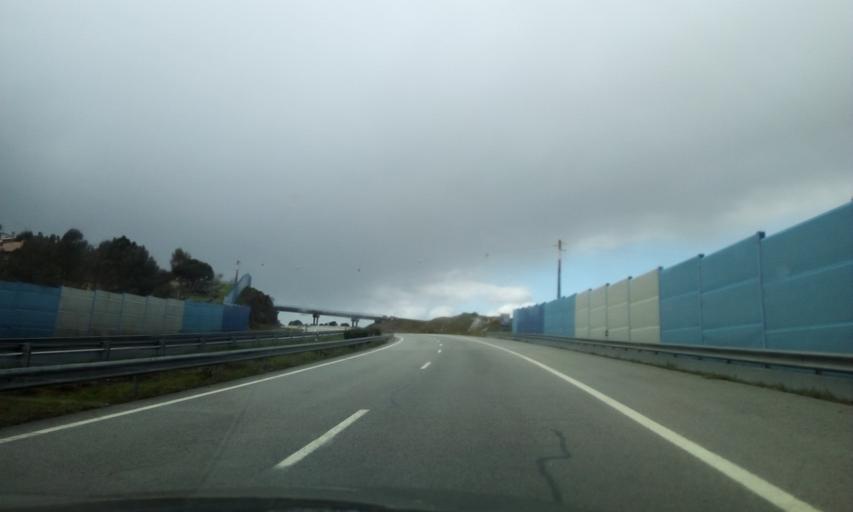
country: PT
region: Viseu
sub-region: Mangualde
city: Mangualde
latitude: 40.6157
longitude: -7.7178
